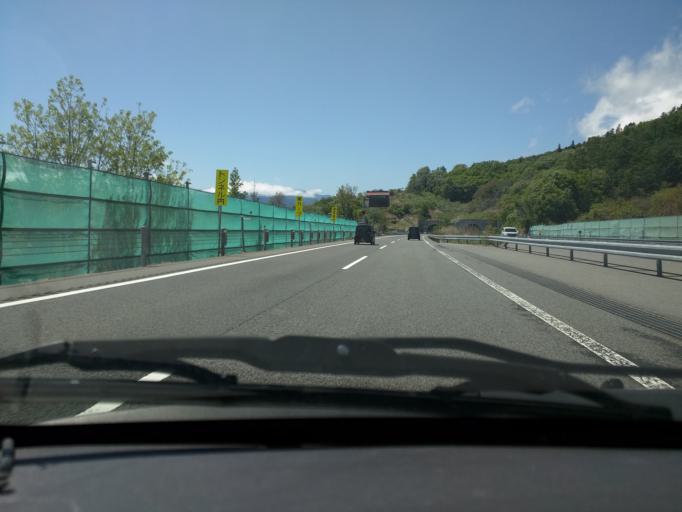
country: JP
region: Nagano
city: Nakano
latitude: 36.7566
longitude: 138.3143
